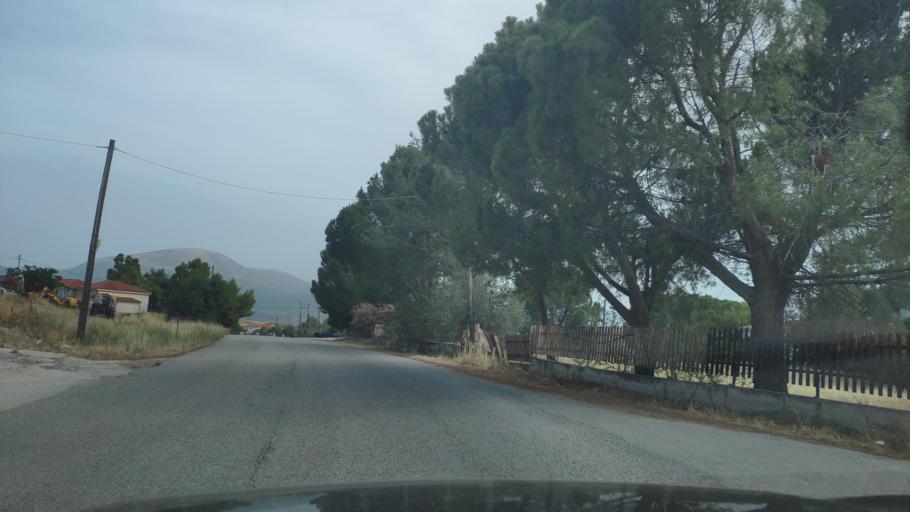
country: GR
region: Peloponnese
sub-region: Nomos Argolidos
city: Palaia Epidavros
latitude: 37.5655
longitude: 23.1501
